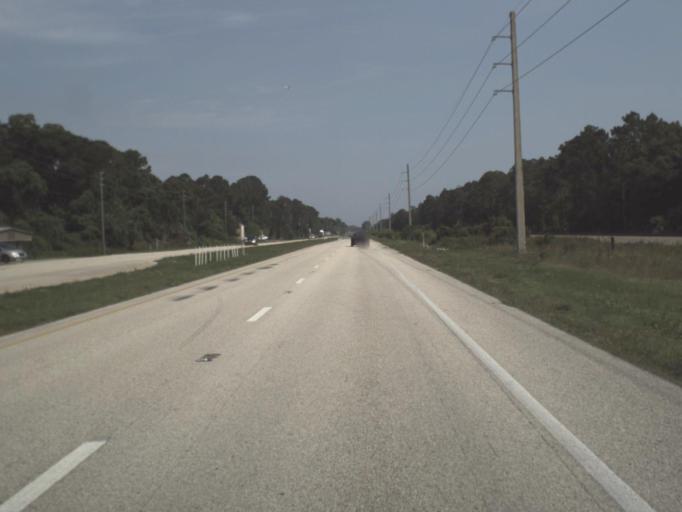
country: US
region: Florida
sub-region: Saint Johns County
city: Villano Beach
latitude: 29.9891
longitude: -81.3712
